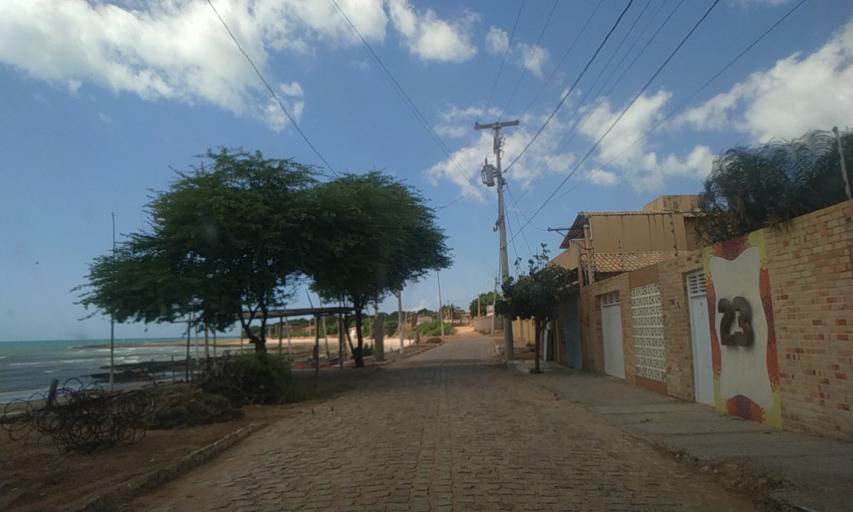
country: BR
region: Rio Grande do Norte
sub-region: Areia Branca
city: Areia Branca
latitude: -4.9257
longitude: -37.1115
